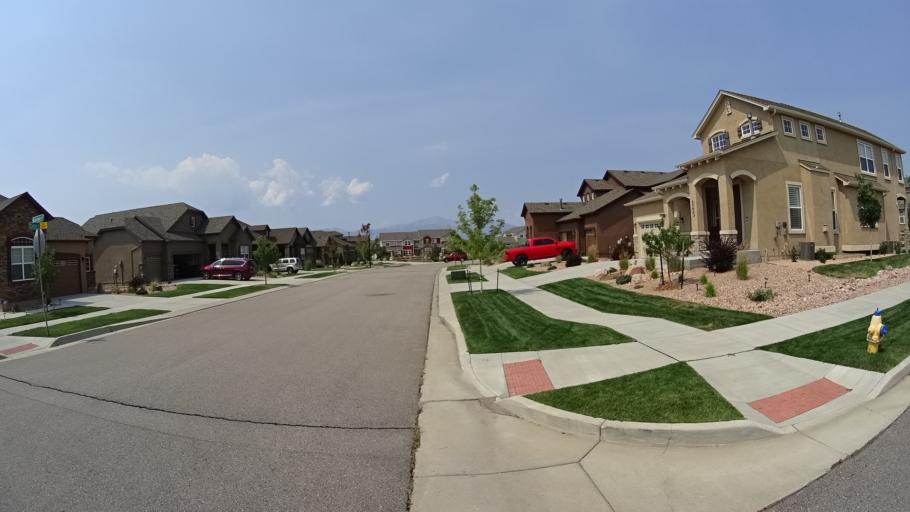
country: US
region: Colorado
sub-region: El Paso County
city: Black Forest
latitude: 38.9615
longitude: -104.7256
